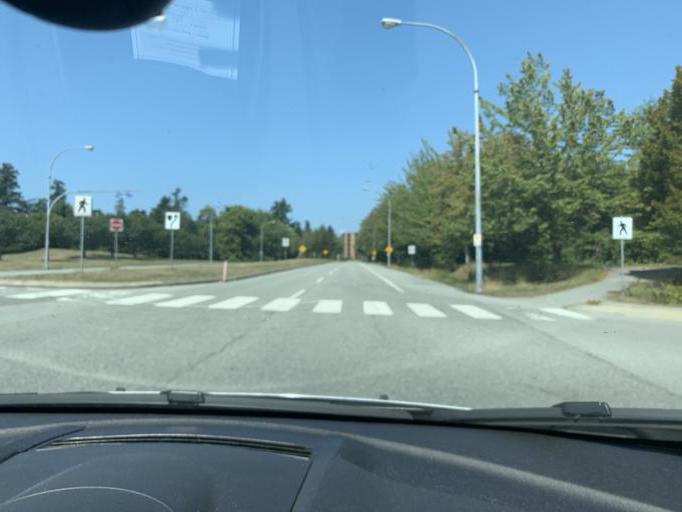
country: CA
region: British Columbia
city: West End
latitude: 49.2545
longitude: -123.2497
